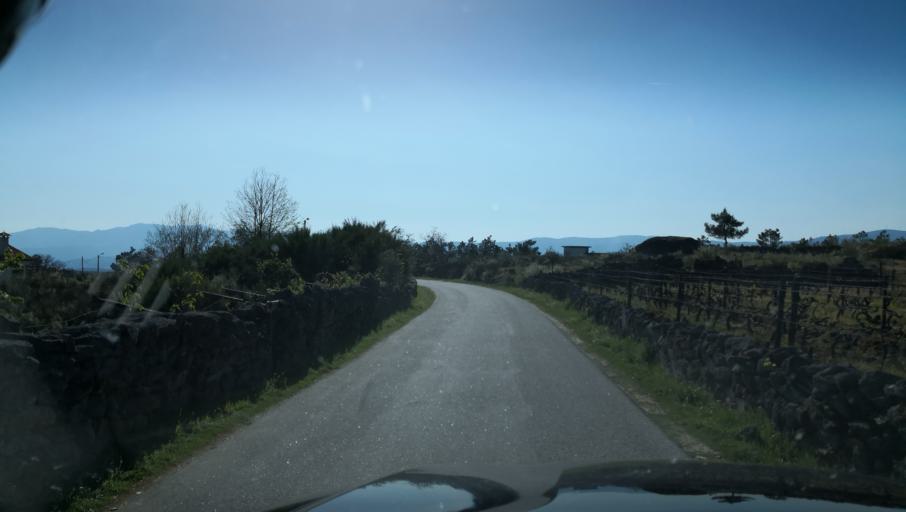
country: PT
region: Vila Real
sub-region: Sabrosa
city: Sabrosa
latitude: 41.2948
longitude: -7.6558
